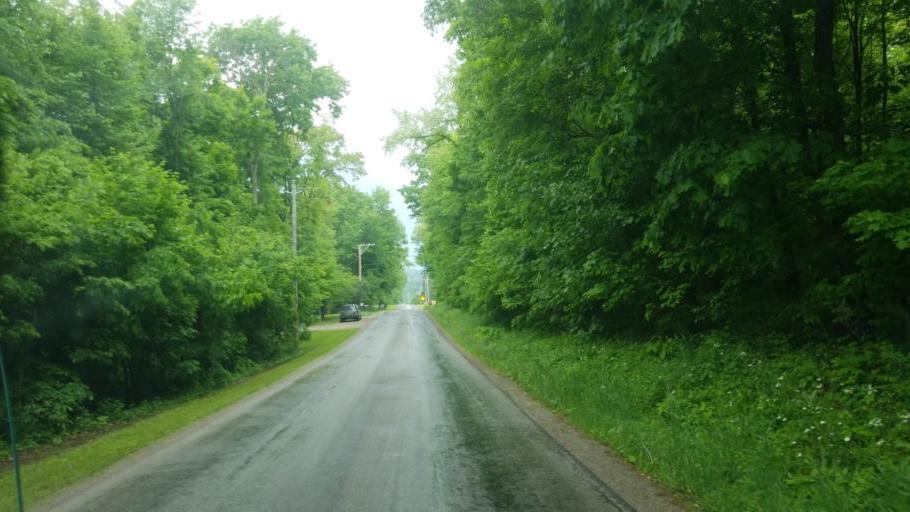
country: US
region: Ohio
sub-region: Wayne County
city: Dalton
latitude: 40.7541
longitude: -81.7065
